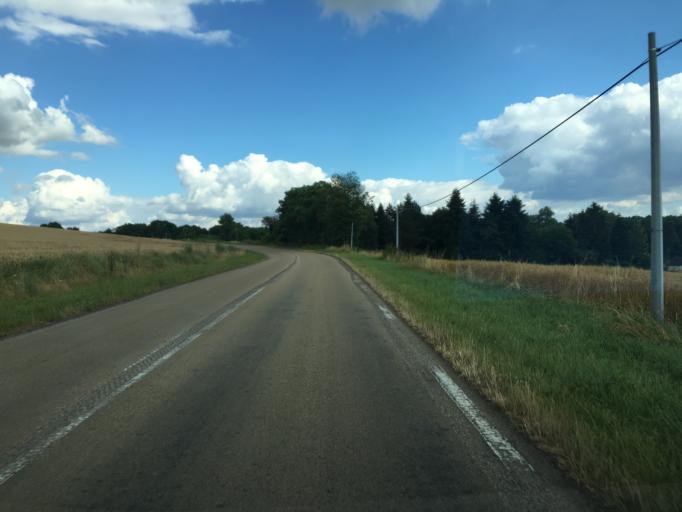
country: FR
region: Bourgogne
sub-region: Departement de l'Yonne
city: Charbuy
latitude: 47.8248
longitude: 3.4241
